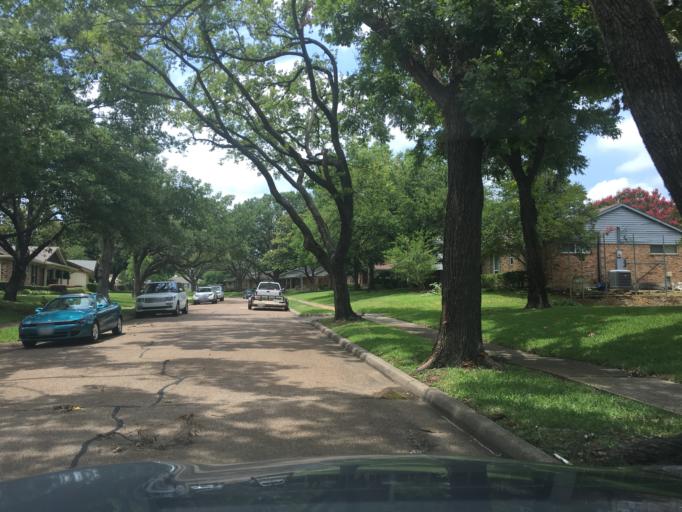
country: US
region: Texas
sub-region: Dallas County
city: Richardson
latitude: 32.9490
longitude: -96.7547
